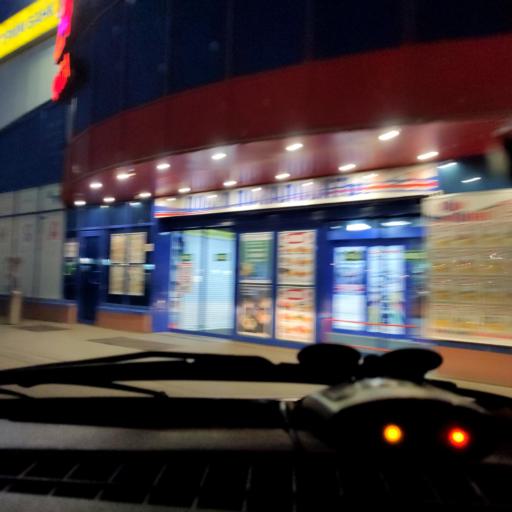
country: RU
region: Voronezj
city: Podgornoye
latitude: 51.7129
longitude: 39.1607
